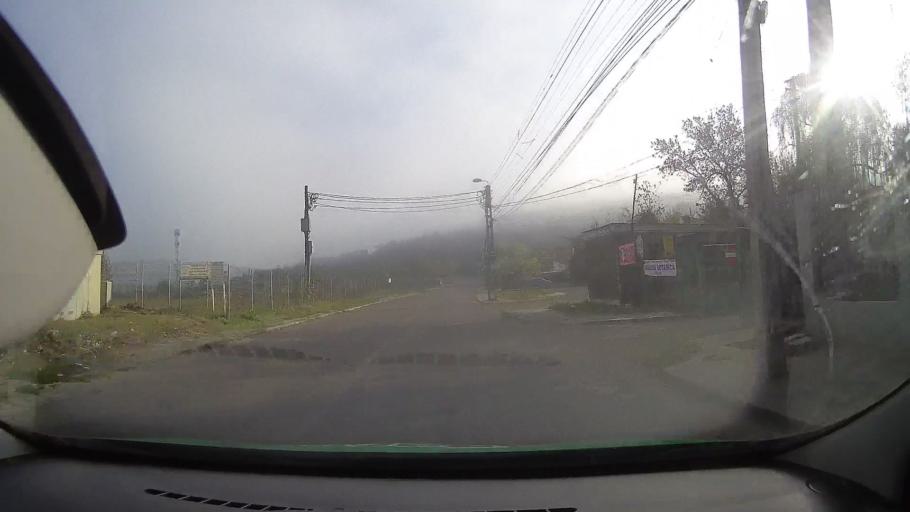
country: RO
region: Tulcea
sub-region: Municipiul Tulcea
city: Tulcea
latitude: 45.1654
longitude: 28.8248
